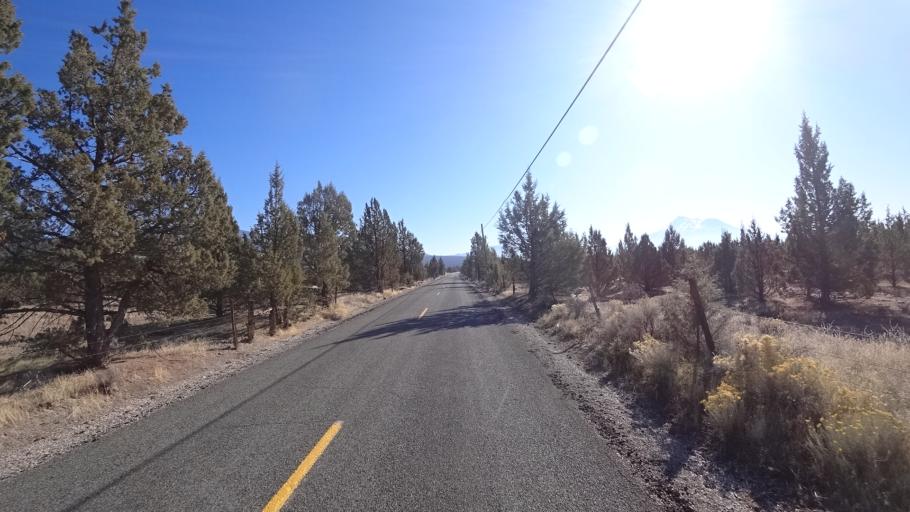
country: US
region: California
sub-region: Siskiyou County
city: Montague
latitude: 41.6443
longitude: -122.3530
